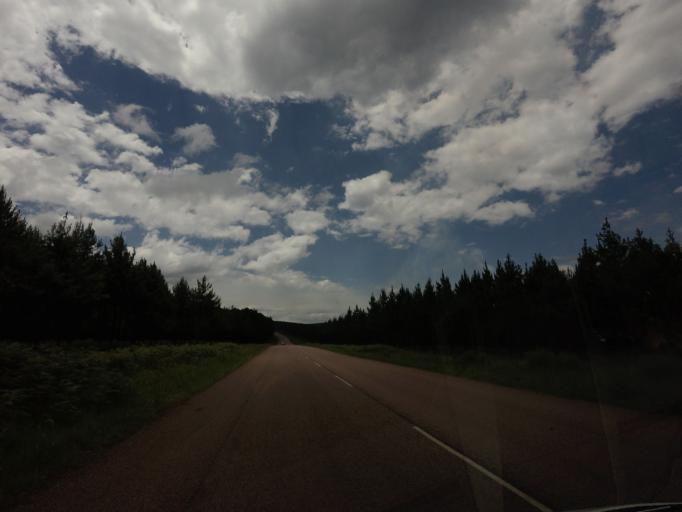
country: ZA
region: Mpumalanga
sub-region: Ehlanzeni District
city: Graksop
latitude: -25.0561
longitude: 30.8178
